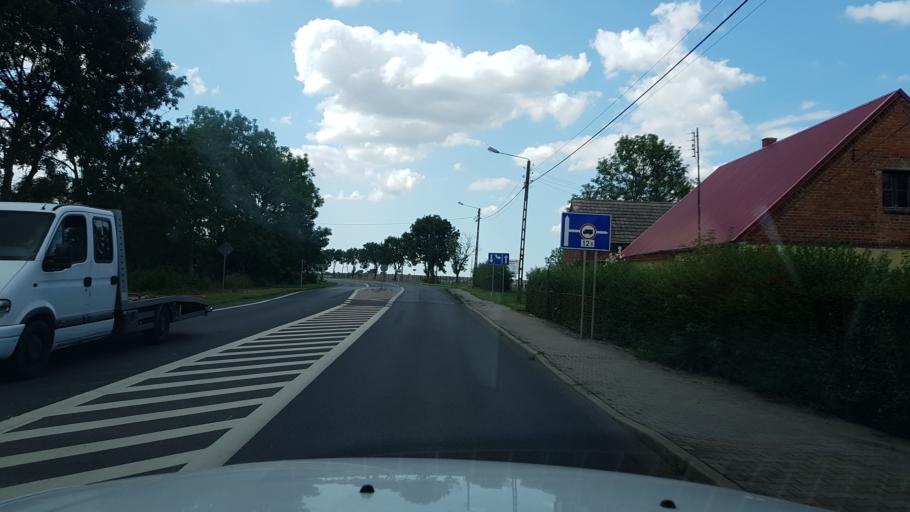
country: PL
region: West Pomeranian Voivodeship
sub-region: Powiat pyrzycki
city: Pyrzyce
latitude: 53.1884
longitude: 14.8386
